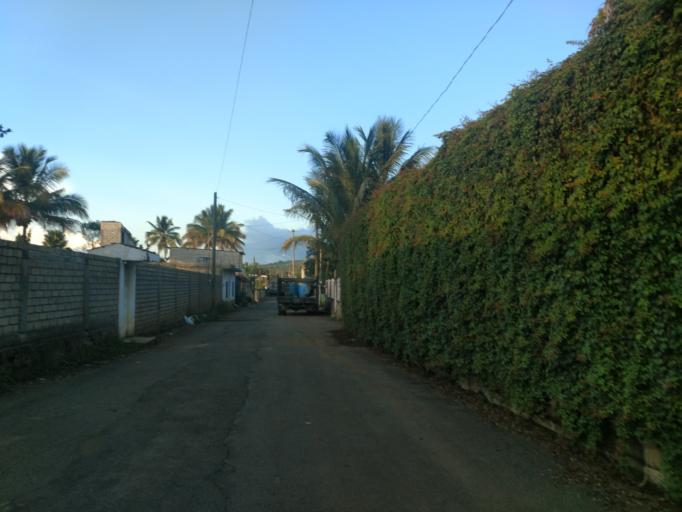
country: MX
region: Nayarit
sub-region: Tepic
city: La Corregidora
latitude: 21.4652
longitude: -104.7995
